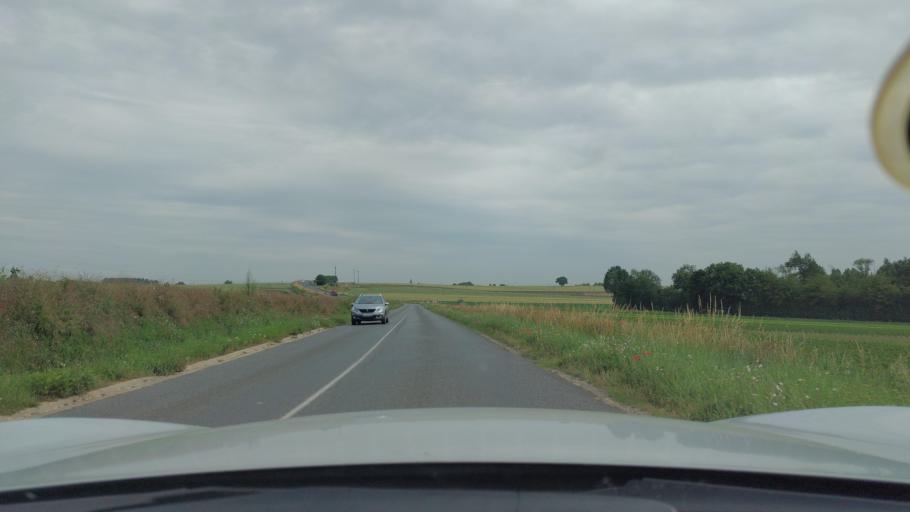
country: FR
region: Ile-de-France
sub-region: Departement de Seine-et-Marne
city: Cregy-les-Meaux
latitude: 49.0030
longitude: 2.8804
